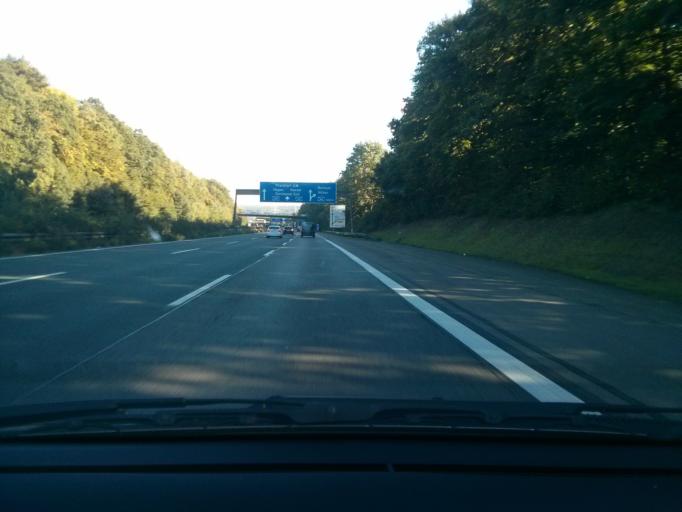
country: DE
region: North Rhine-Westphalia
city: Witten
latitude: 51.4716
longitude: 7.3992
